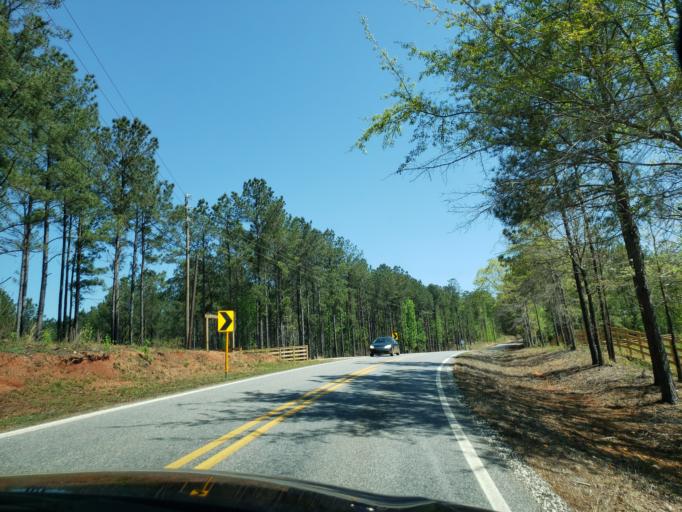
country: US
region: Alabama
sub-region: Elmore County
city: Tallassee
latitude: 32.6844
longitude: -85.8704
